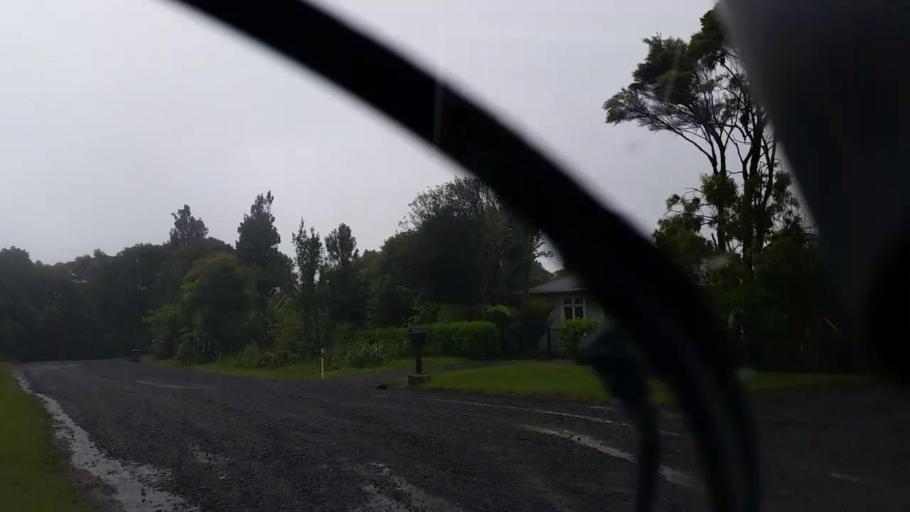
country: NZ
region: Auckland
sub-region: Auckland
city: Waitakere
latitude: -36.9108
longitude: 174.5462
